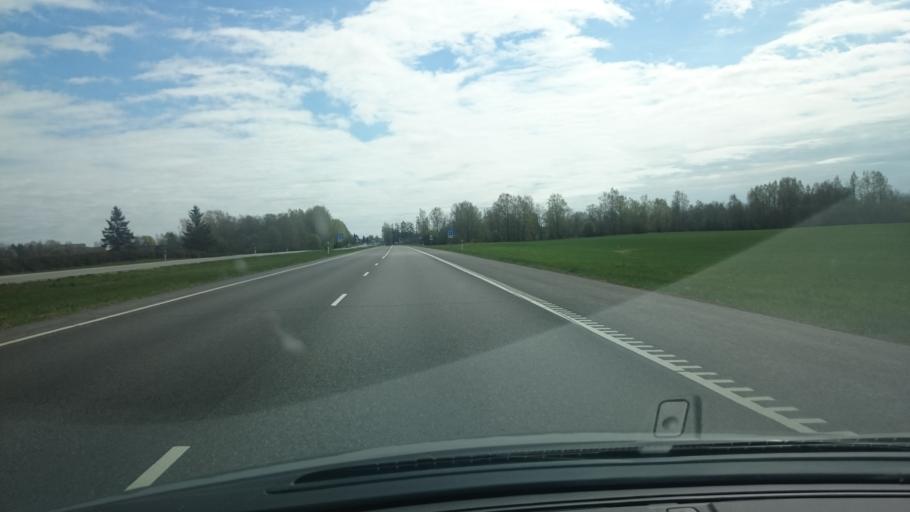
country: EE
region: Laeaene-Virumaa
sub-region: Kadrina vald
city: Kadrina
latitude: 59.4400
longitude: 26.1233
